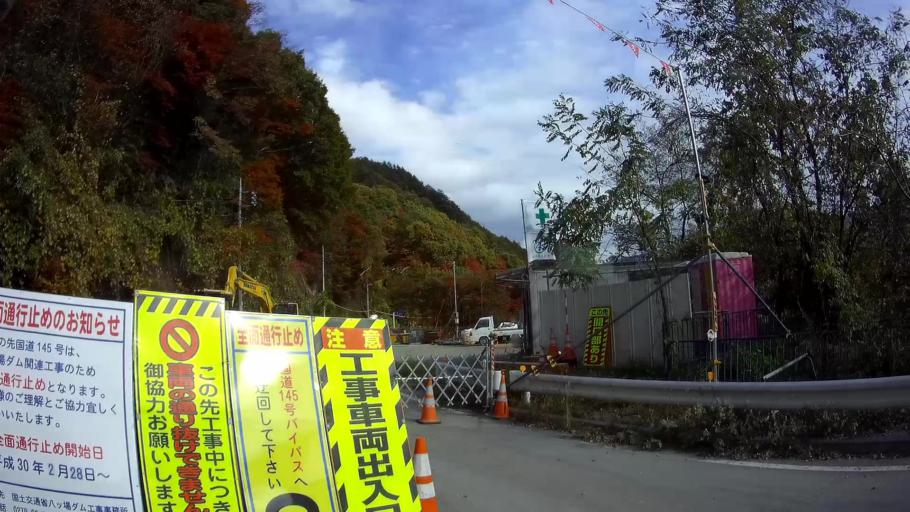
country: JP
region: Gunma
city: Nakanojomachi
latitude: 36.5462
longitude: 138.6553
